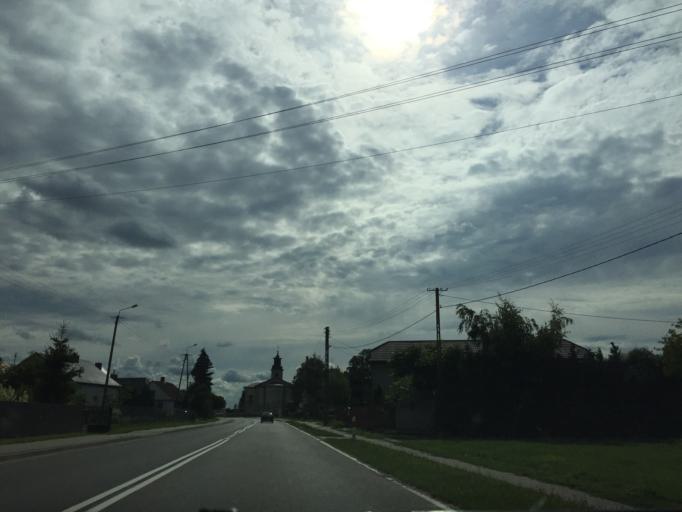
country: PL
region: Lublin Voivodeship
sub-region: Powiat lukowski
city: Trzebieszow
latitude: 51.9885
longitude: 22.5474
